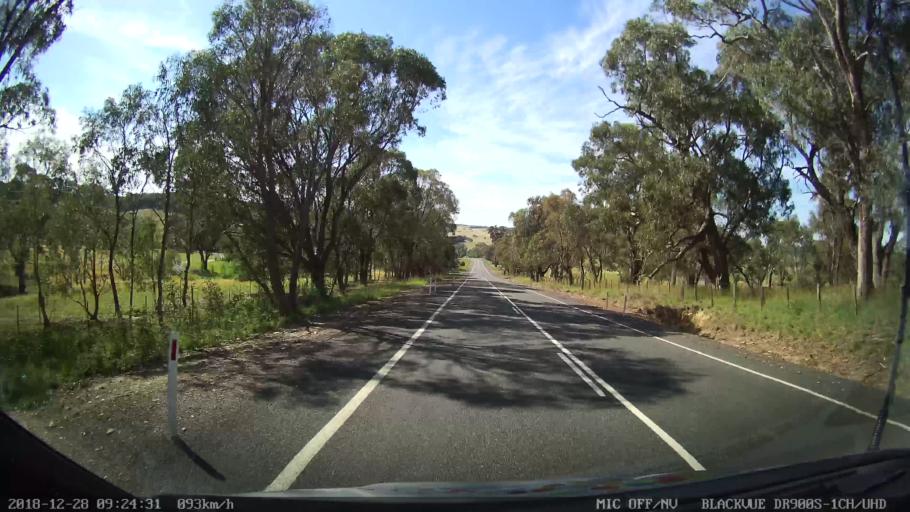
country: AU
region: New South Wales
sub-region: Upper Lachlan Shire
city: Crookwell
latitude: -34.3986
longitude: 149.3811
